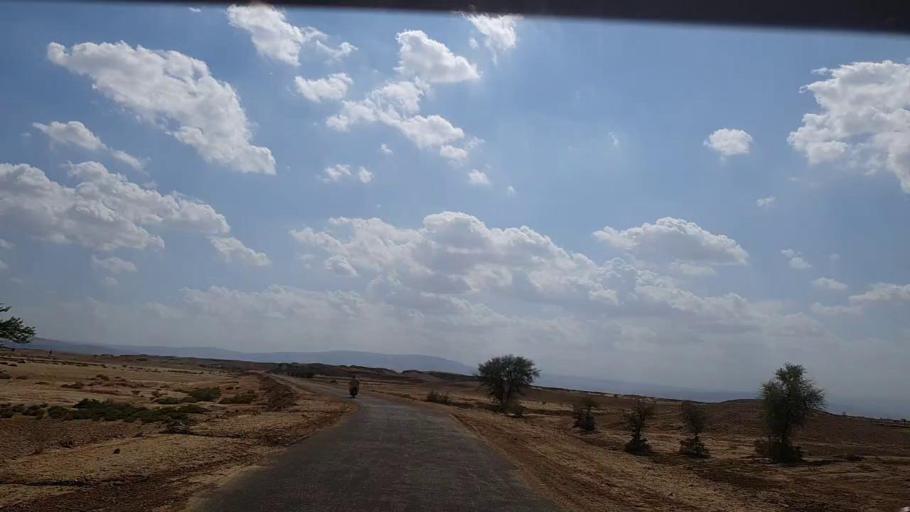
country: PK
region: Sindh
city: Johi
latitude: 26.5275
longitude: 67.5157
